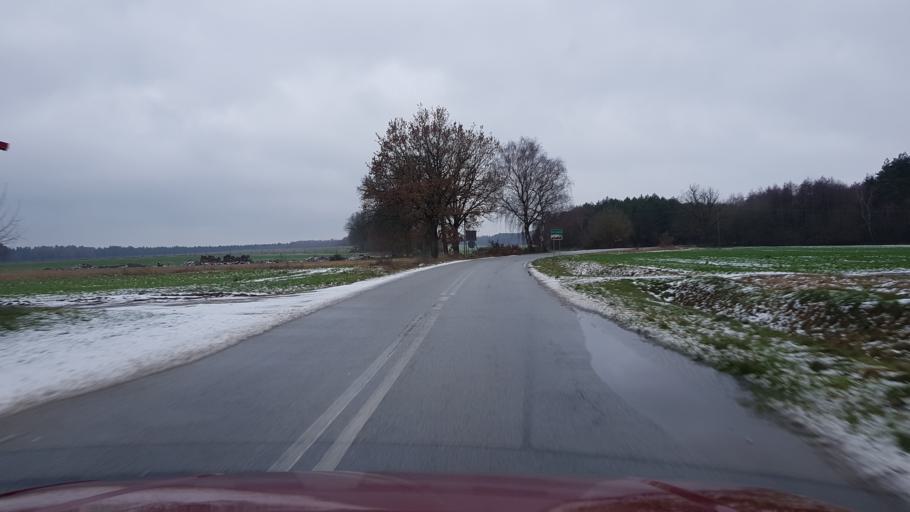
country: PL
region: West Pomeranian Voivodeship
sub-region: Powiat gryficki
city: Ploty
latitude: 53.6989
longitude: 15.2698
